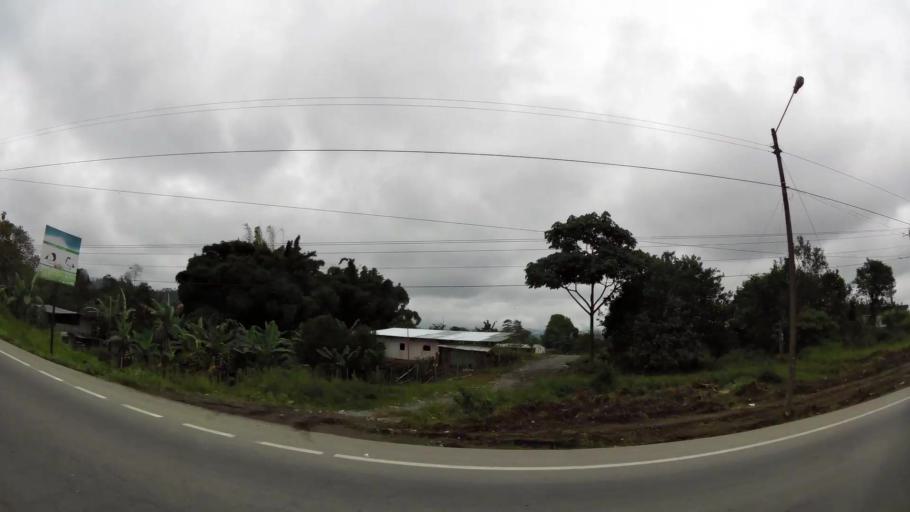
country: EC
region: Santo Domingo de los Tsachilas
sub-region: Canton Santo Domingo de los Colorados
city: Santo Domingo de los Colorados
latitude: -0.2771
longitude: -79.1716
